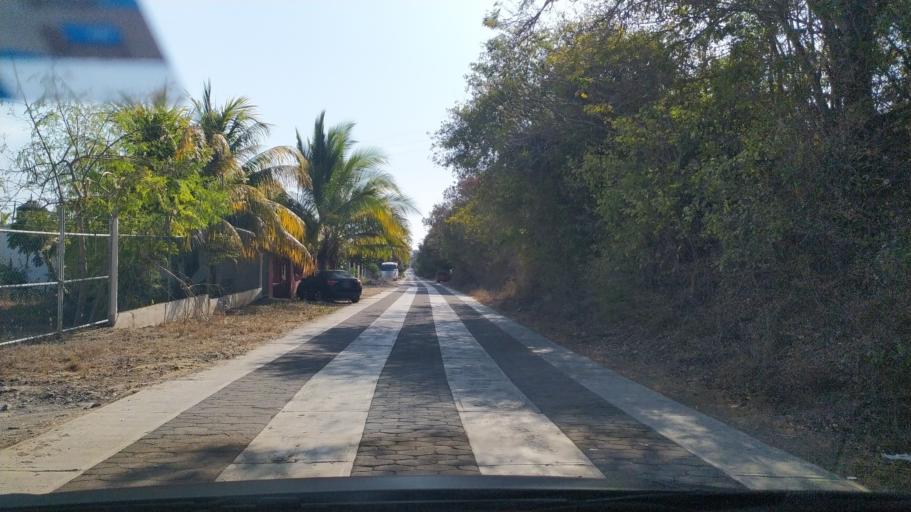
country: MX
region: Michoacan
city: Coahuayana Viejo
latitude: 18.5868
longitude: -103.6715
